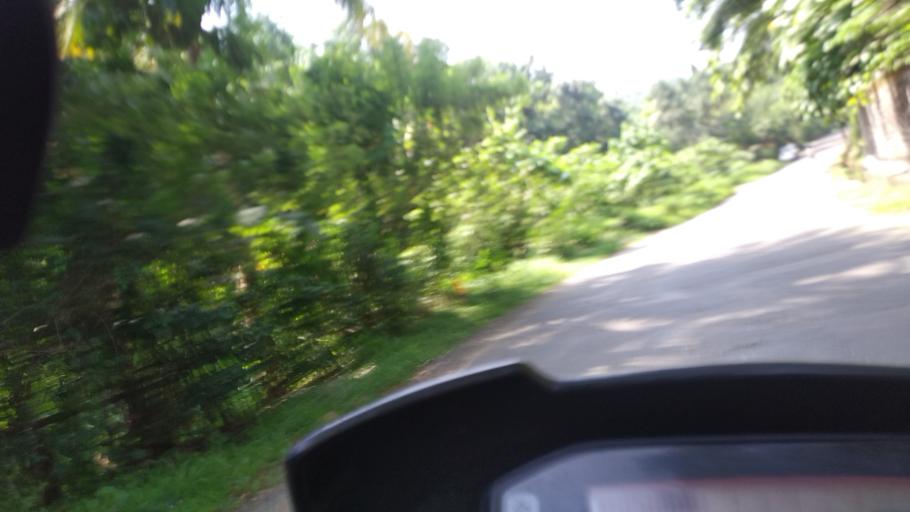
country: IN
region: Kerala
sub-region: Kottayam
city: Erattupetta
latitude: 9.6955
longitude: 76.8241
